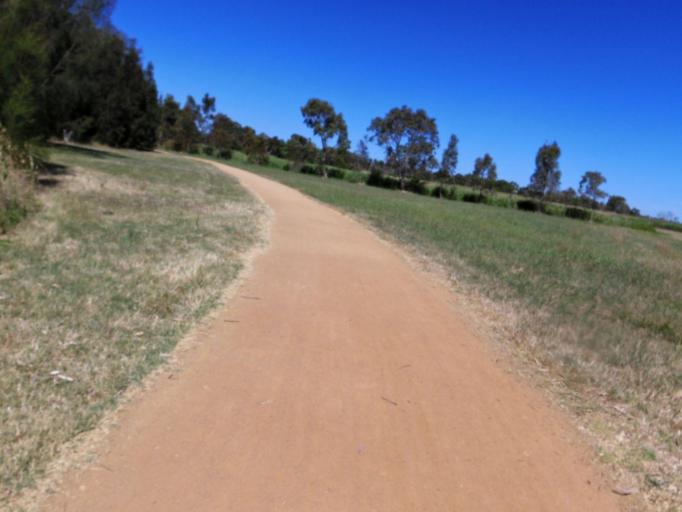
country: AU
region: Victoria
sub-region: Kingston
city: Chelsea
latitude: -38.0491
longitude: 145.1323
